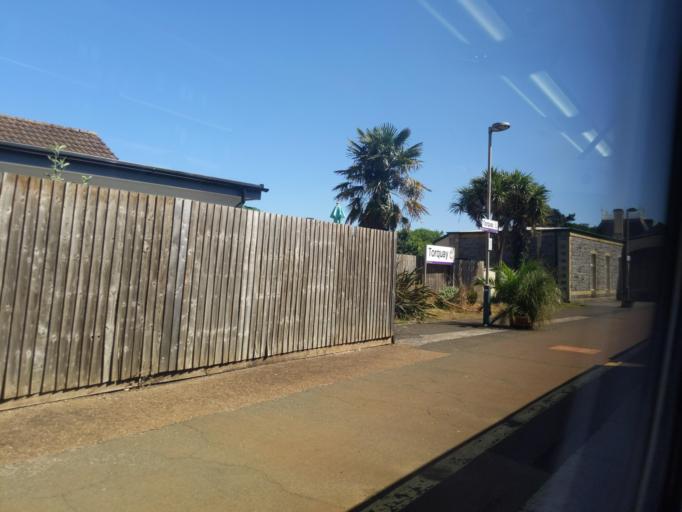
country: GB
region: England
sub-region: Borough of Torbay
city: Torquay
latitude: 50.4619
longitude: -3.5435
